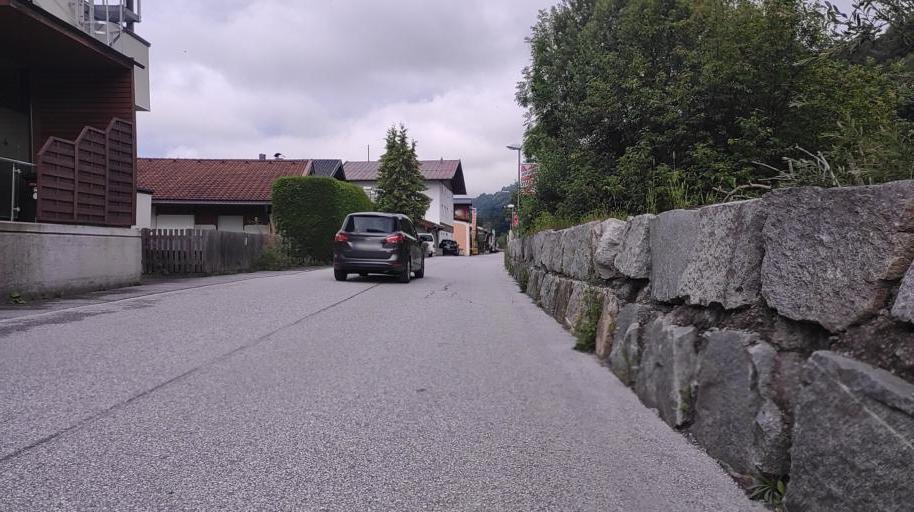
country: AT
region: Salzburg
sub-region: Politischer Bezirk Zell am See
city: Mittersill
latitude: 47.2832
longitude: 12.4791
